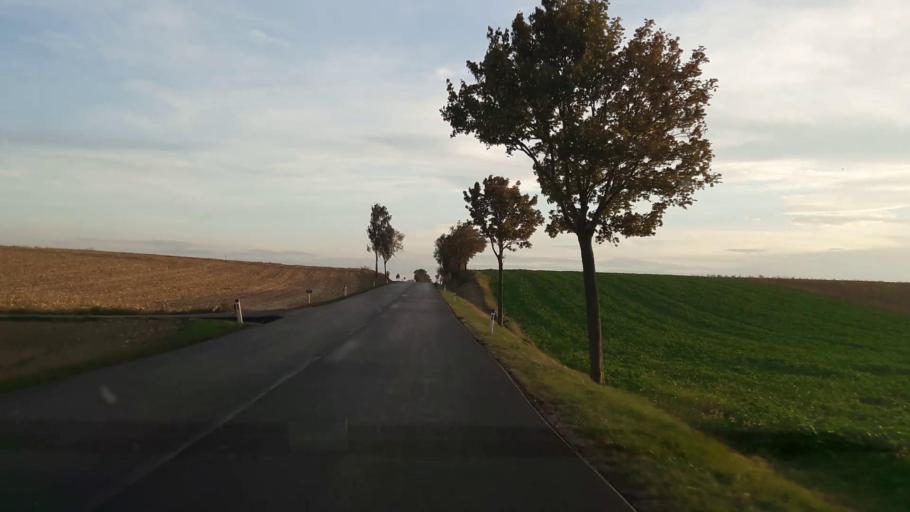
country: AT
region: Lower Austria
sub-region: Politischer Bezirk Korneuburg
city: Grossrussbach
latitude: 48.4707
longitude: 16.3796
